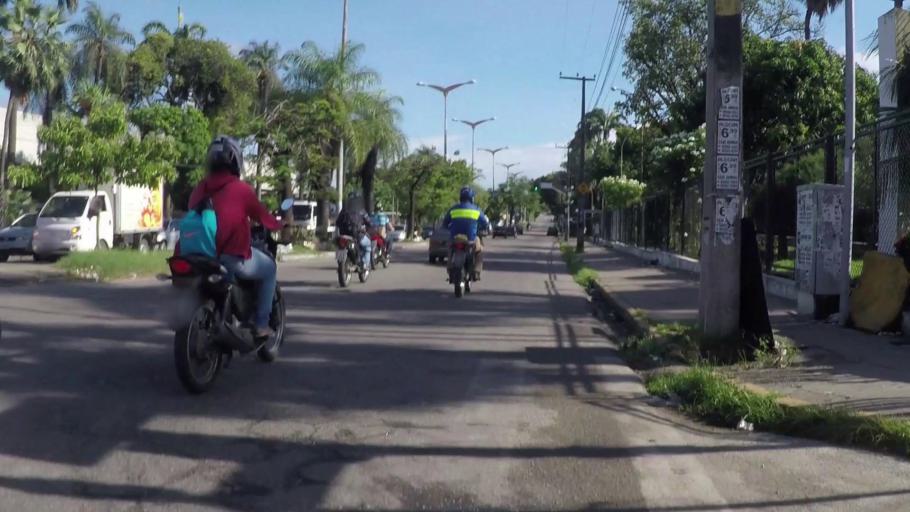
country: BR
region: Ceara
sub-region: Fortaleza
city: Fortaleza
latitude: -3.7338
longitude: -38.5843
